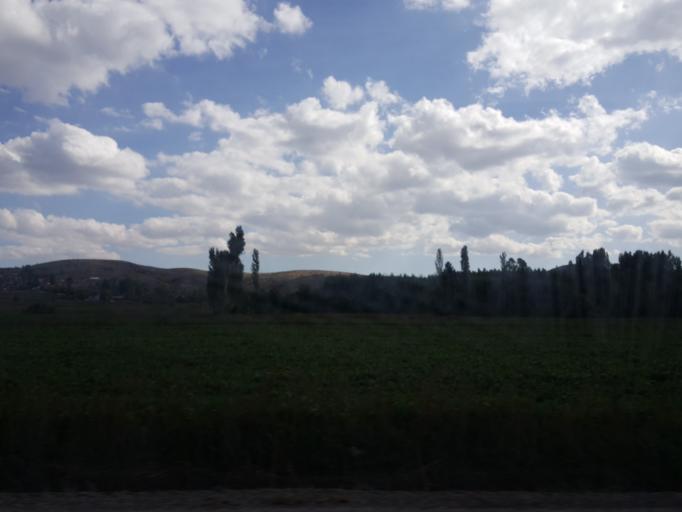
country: TR
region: Tokat
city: Yesilyurt
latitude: 40.0255
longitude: 36.2929
